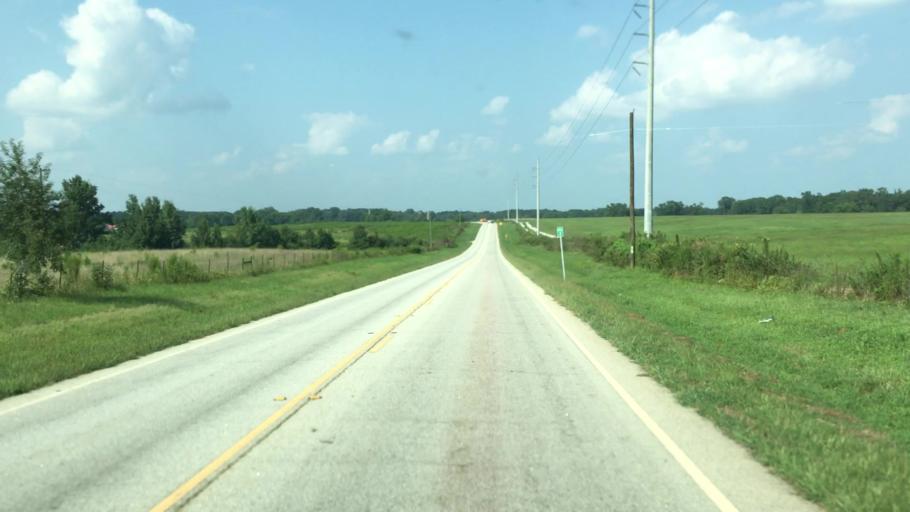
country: US
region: Georgia
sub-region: Newton County
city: Covington
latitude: 33.4926
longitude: -83.7392
